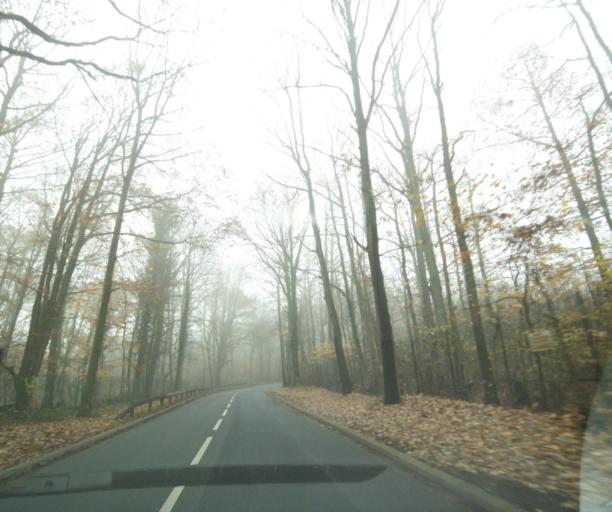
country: FR
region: Ile-de-France
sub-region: Departement de Seine-Saint-Denis
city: Vaujours
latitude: 48.9249
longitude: 2.5747
